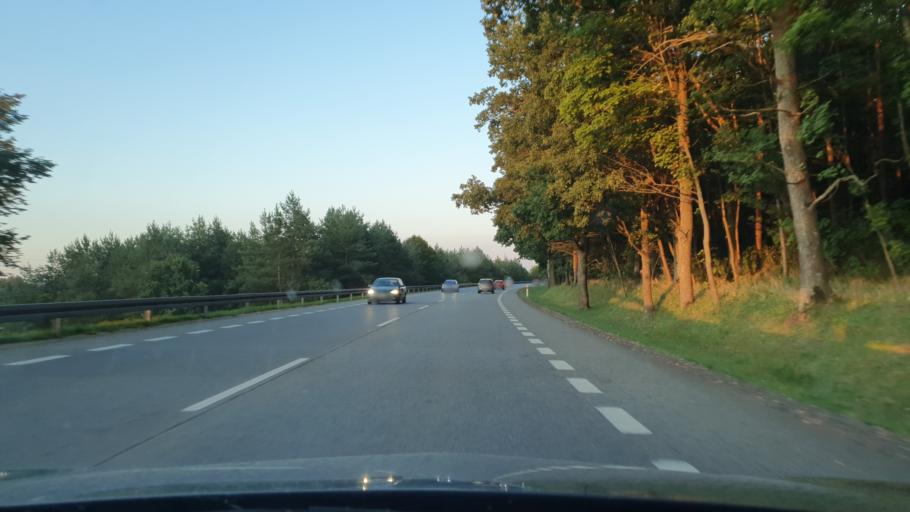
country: PL
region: Pomeranian Voivodeship
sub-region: Powiat leborski
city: Nowa Wies Leborska
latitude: 54.5228
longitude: 17.6904
